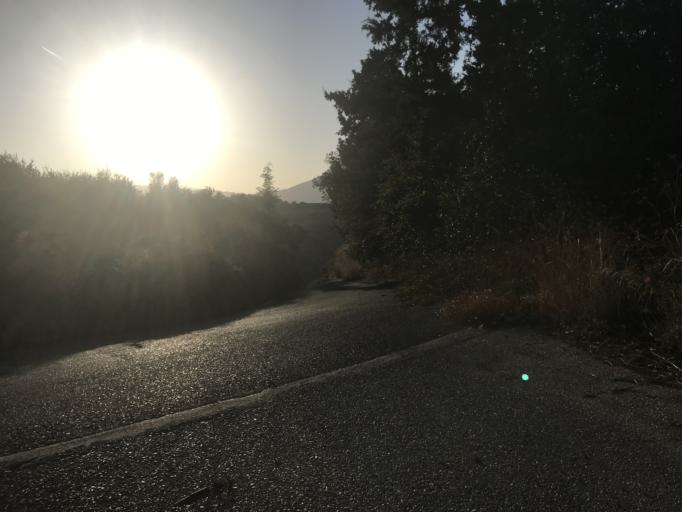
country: GR
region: Crete
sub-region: Nomos Irakleiou
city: Gazi
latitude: 35.3069
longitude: 25.0732
